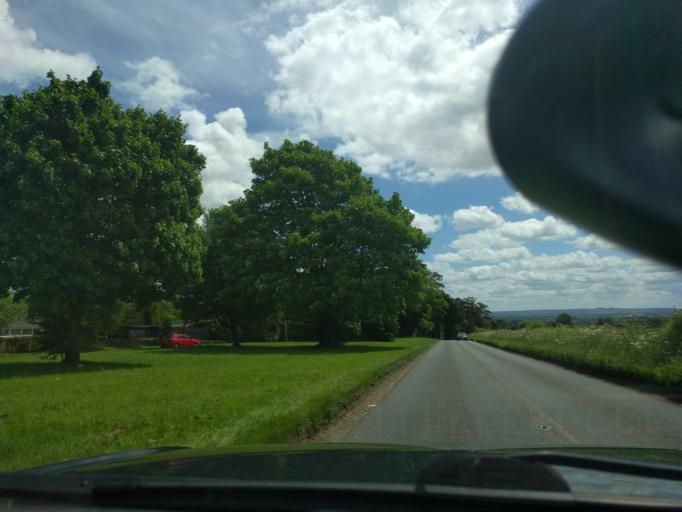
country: GB
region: England
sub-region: Wiltshire
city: Corsham
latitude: 51.4112
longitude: -2.1674
